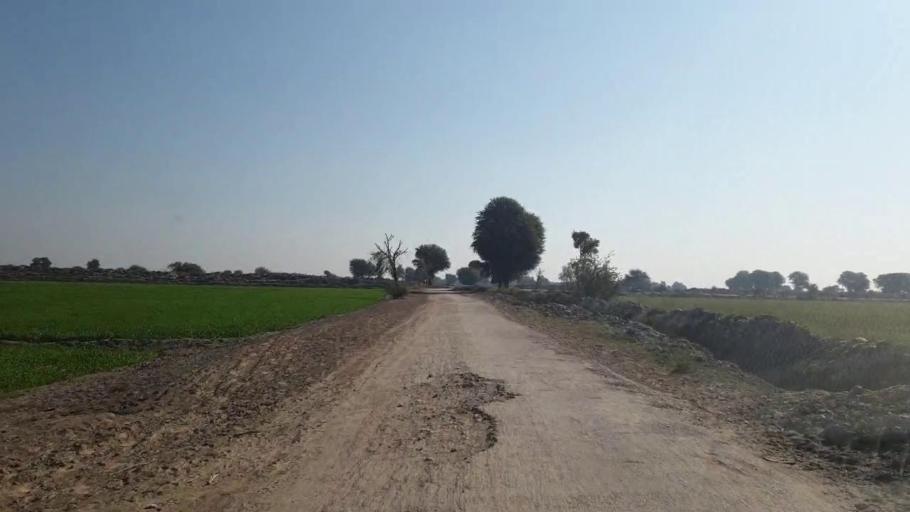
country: PK
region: Sindh
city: Shahpur Chakar
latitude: 26.0895
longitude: 68.6457
